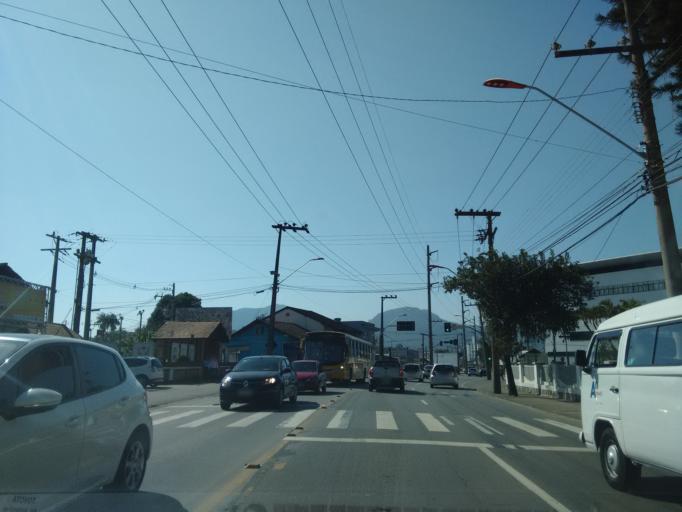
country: BR
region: Santa Catarina
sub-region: Jaragua Do Sul
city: Jaragua do Sul
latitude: -26.5033
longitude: -49.0902
